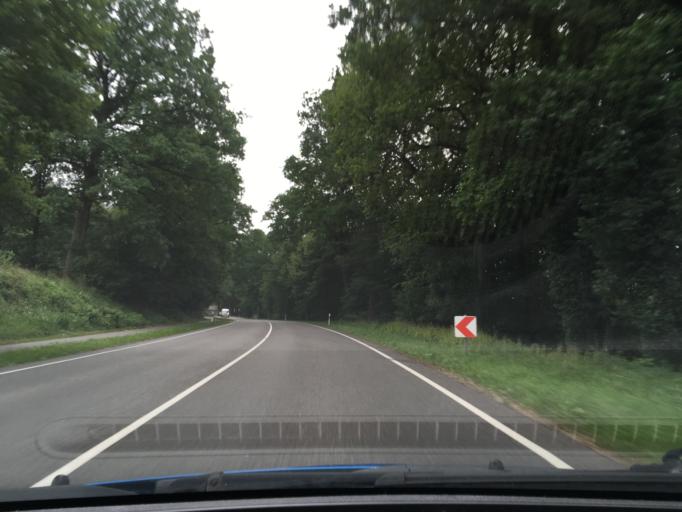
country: DE
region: Lower Saxony
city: Appel
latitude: 53.4010
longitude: 9.7887
